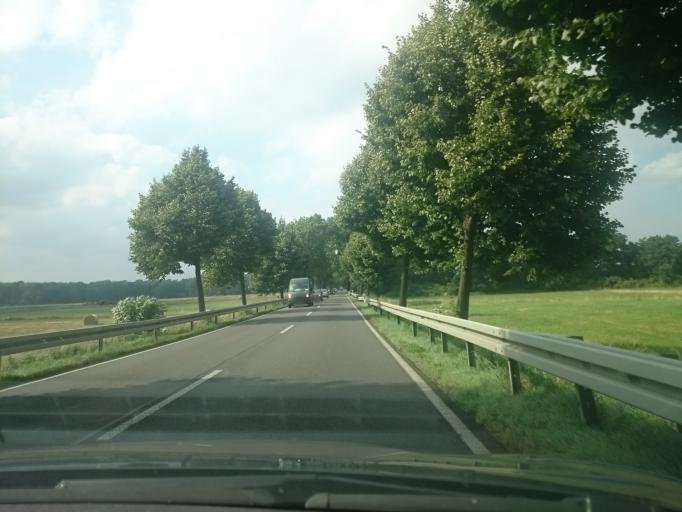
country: DE
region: Mecklenburg-Vorpommern
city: Ducherow
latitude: 53.7267
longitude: 13.8129
